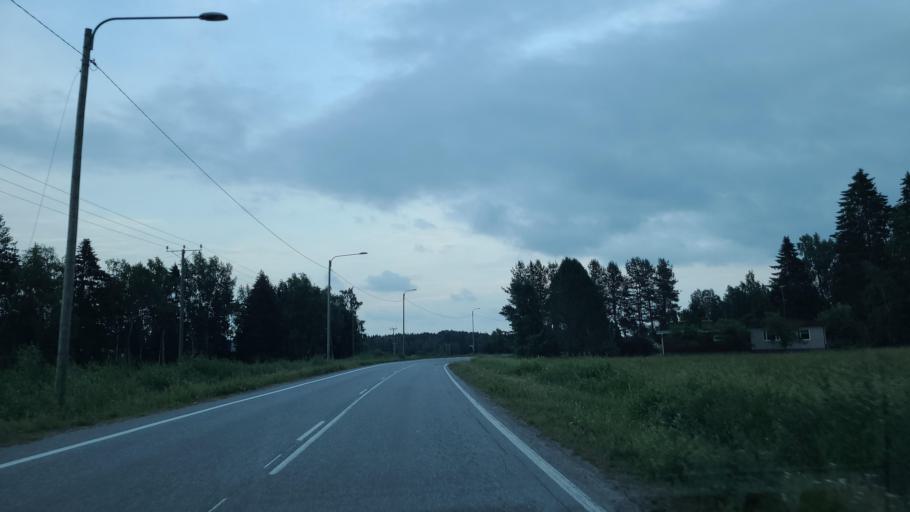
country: FI
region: Ostrobothnia
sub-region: Vaasa
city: Replot
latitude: 63.2012
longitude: 21.3005
